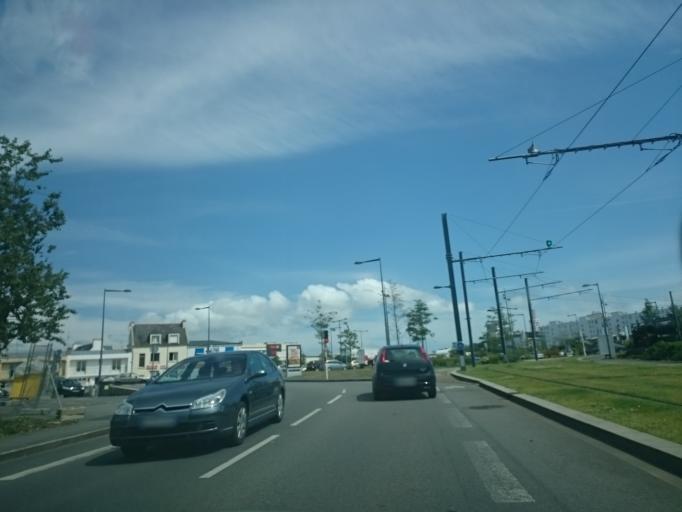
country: FR
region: Brittany
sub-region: Departement du Finistere
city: Brest
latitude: 48.4091
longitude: -4.4694
